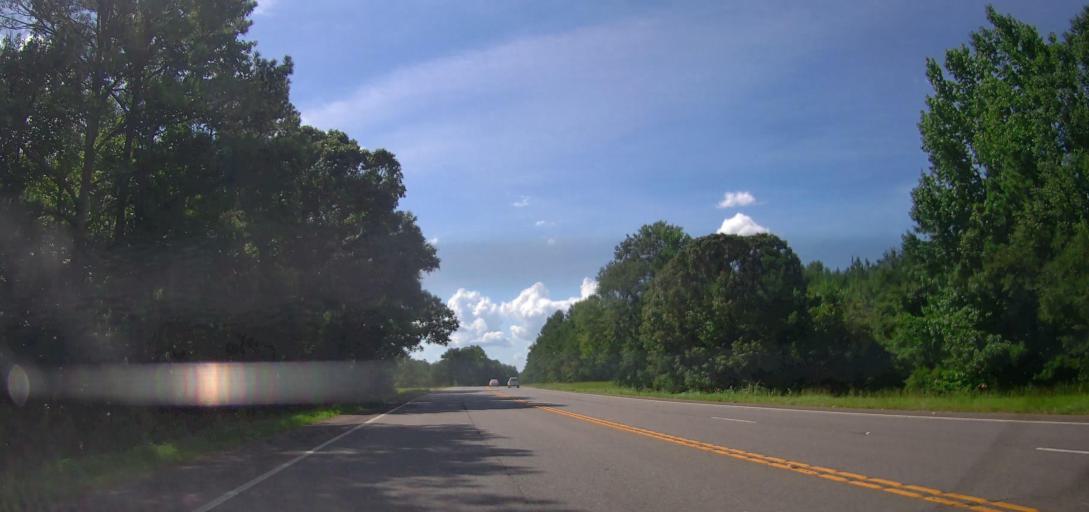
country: US
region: Alabama
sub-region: Pickens County
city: Gordo
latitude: 33.2888
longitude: -87.8674
